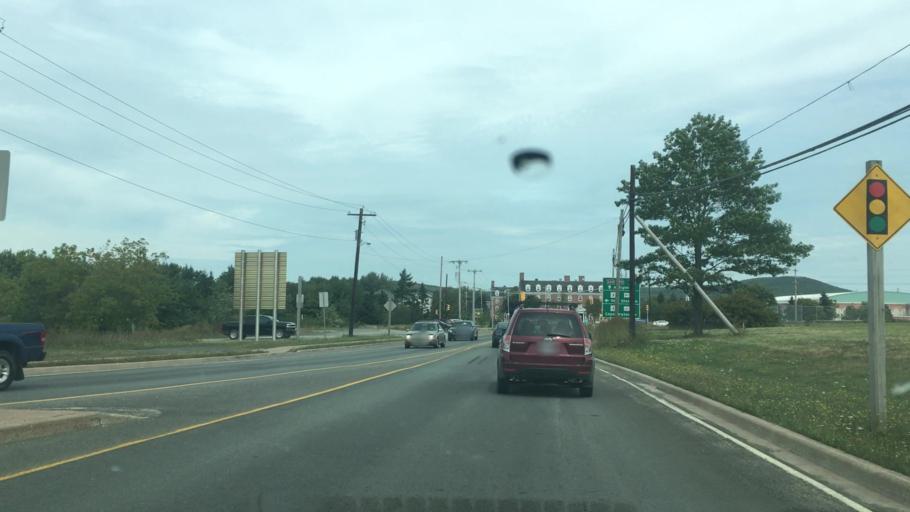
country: CA
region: Nova Scotia
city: Antigonish
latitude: 45.6126
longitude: -61.9989
